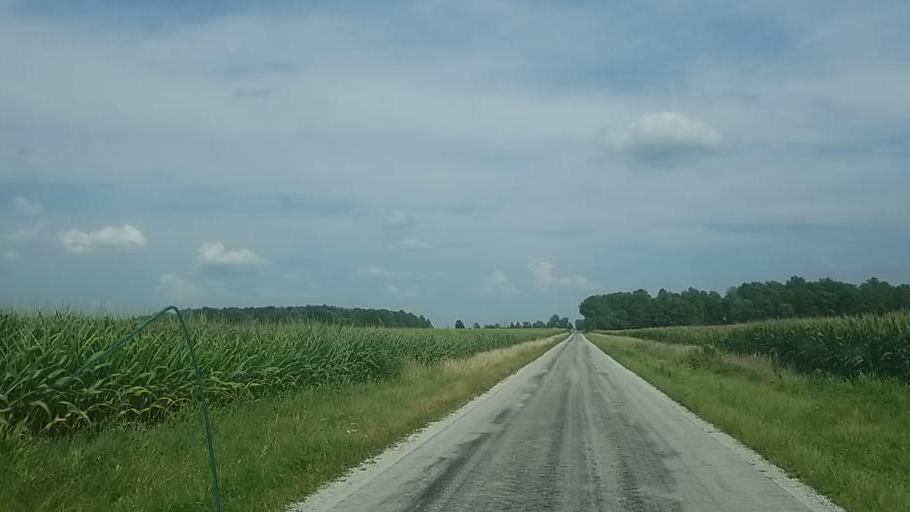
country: US
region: Ohio
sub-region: Hardin County
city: Forest
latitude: 40.8176
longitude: -83.4474
